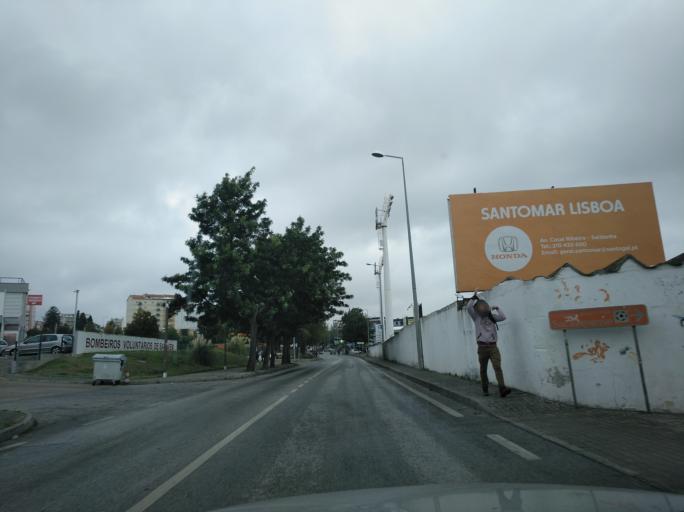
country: PT
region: Lisbon
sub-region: Loures
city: Sacavem
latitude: 38.7890
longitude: -9.1036
